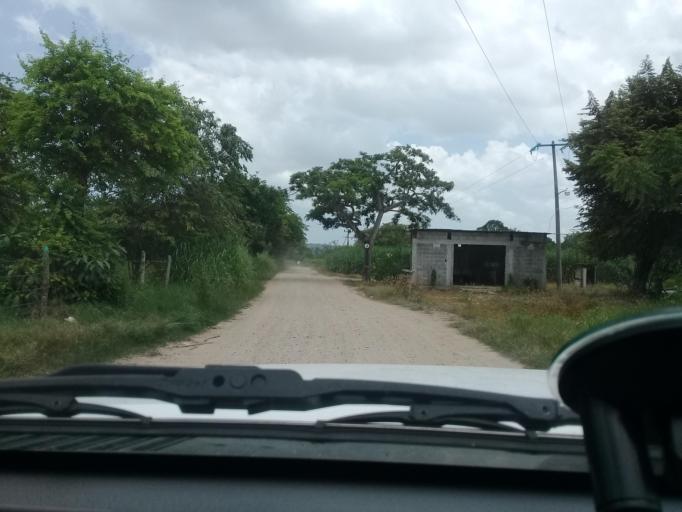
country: MX
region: Veracruz
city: Panuco
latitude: 22.1301
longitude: -98.0646
